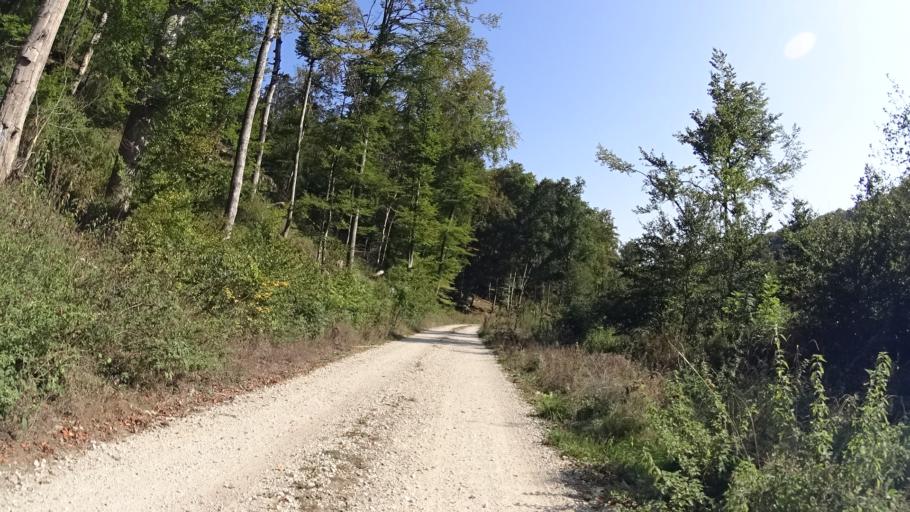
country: DE
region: Bavaria
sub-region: Upper Bavaria
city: Walting
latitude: 48.9188
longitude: 11.2730
